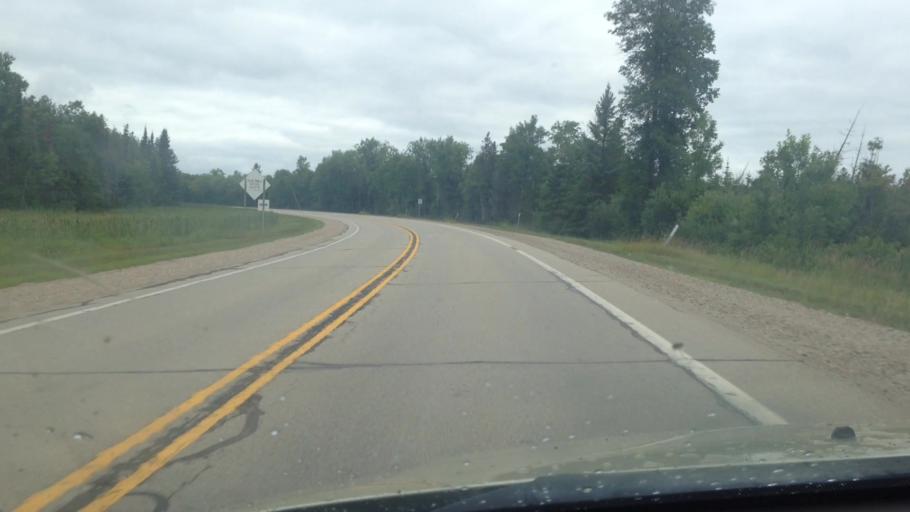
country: US
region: Michigan
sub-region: Menominee County
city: Menominee
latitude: 45.4183
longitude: -87.3465
